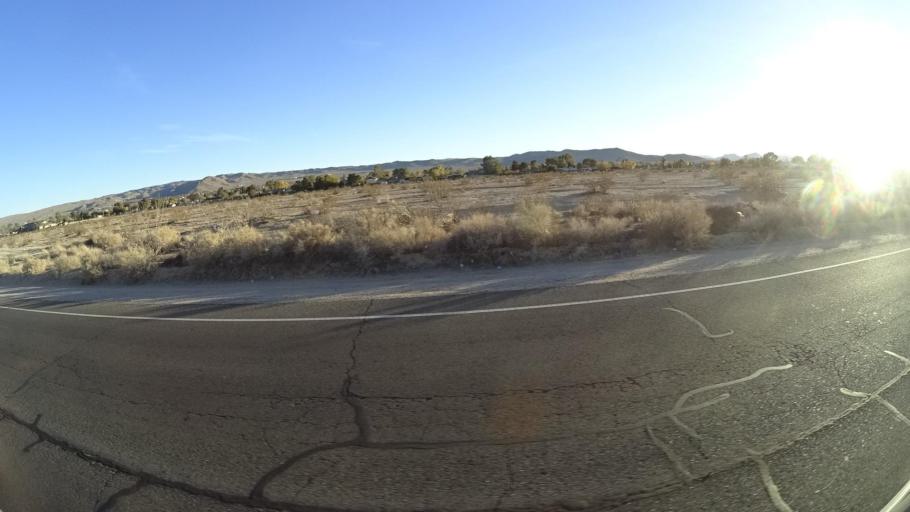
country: US
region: California
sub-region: Kern County
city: Ridgecrest
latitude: 35.6082
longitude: -117.6859
